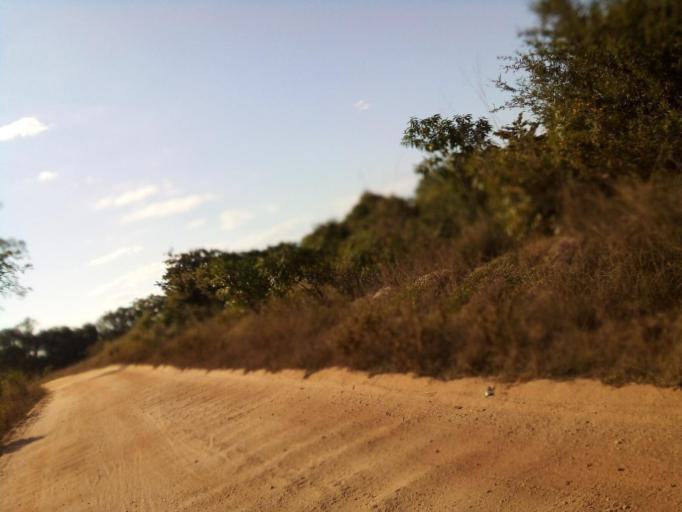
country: MZ
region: Zambezia
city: Quelimane
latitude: -17.5448
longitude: 36.6272
